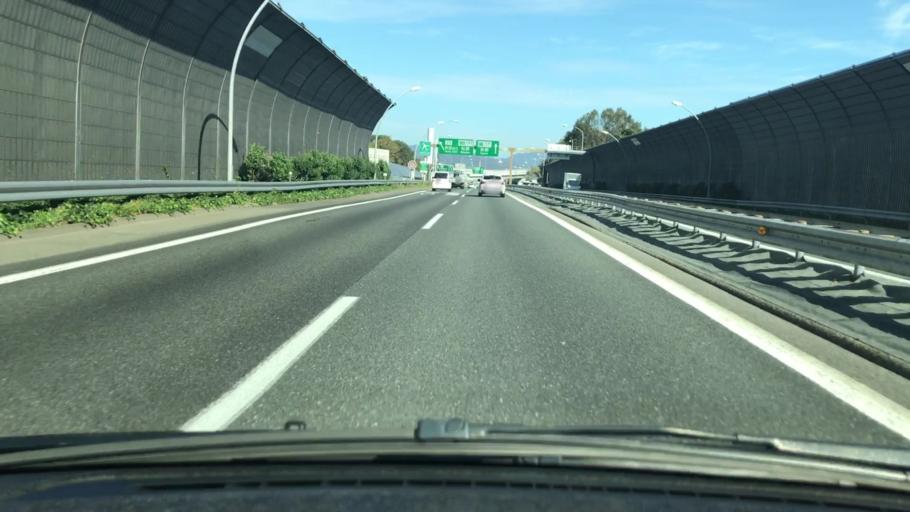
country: JP
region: Osaka
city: Ibaraki
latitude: 34.7986
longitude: 135.5393
